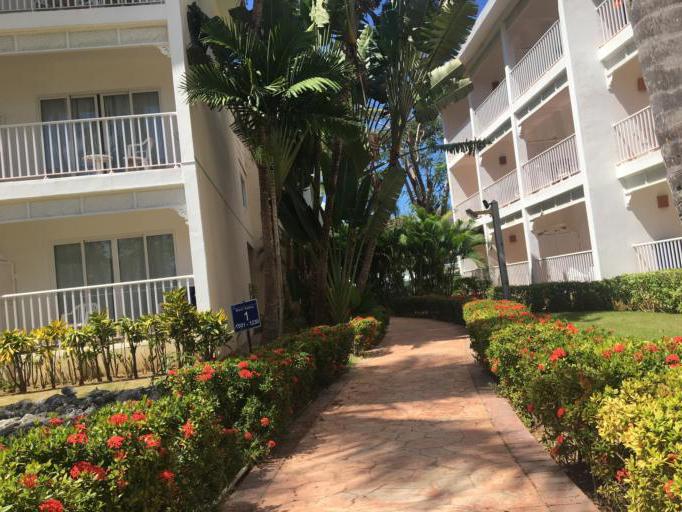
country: DO
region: San Juan
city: Punta Cana
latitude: 18.7086
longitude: -68.4439
